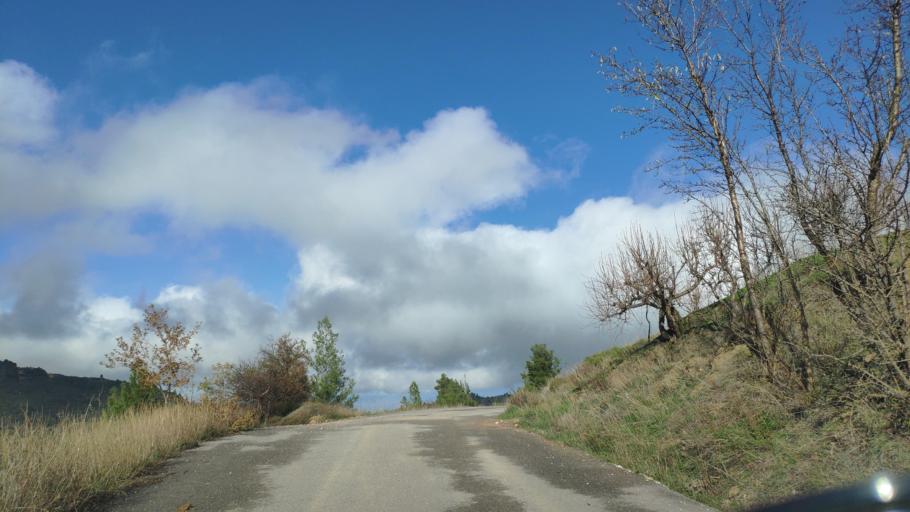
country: GR
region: West Greece
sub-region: Nomos Achaias
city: Aiyira
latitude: 38.0727
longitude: 22.4680
